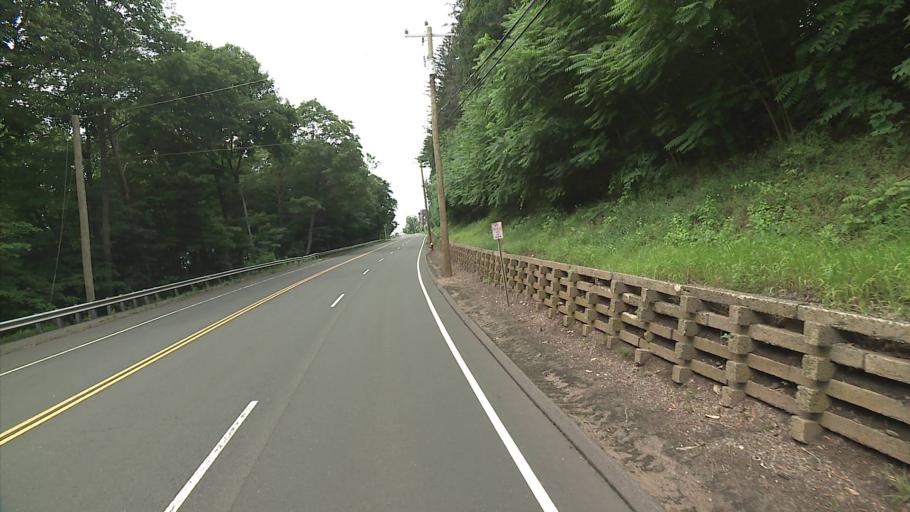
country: US
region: Connecticut
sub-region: Middlesex County
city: Cromwell
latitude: 41.6068
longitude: -72.6492
